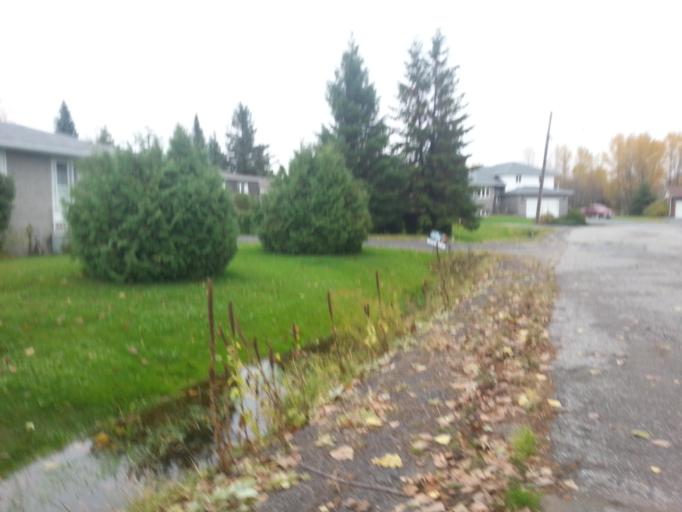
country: CA
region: Ontario
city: Greater Sudbury
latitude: 46.5430
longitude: -81.0967
